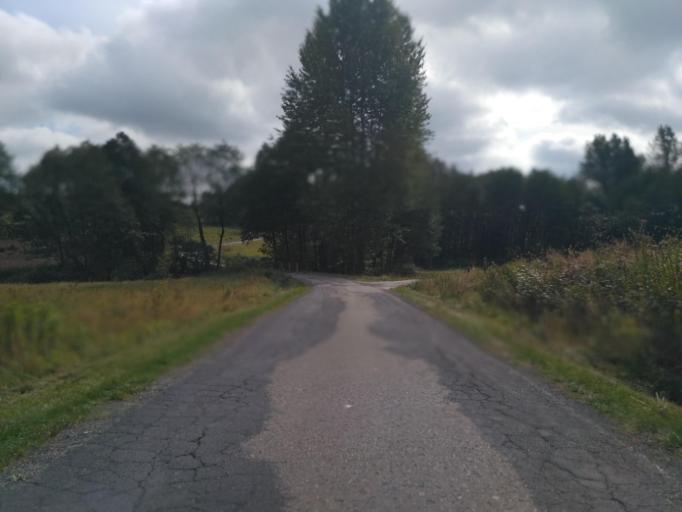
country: PL
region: Subcarpathian Voivodeship
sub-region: Powiat ropczycko-sedziszowski
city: Niedzwiada
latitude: 49.9350
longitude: 21.4689
